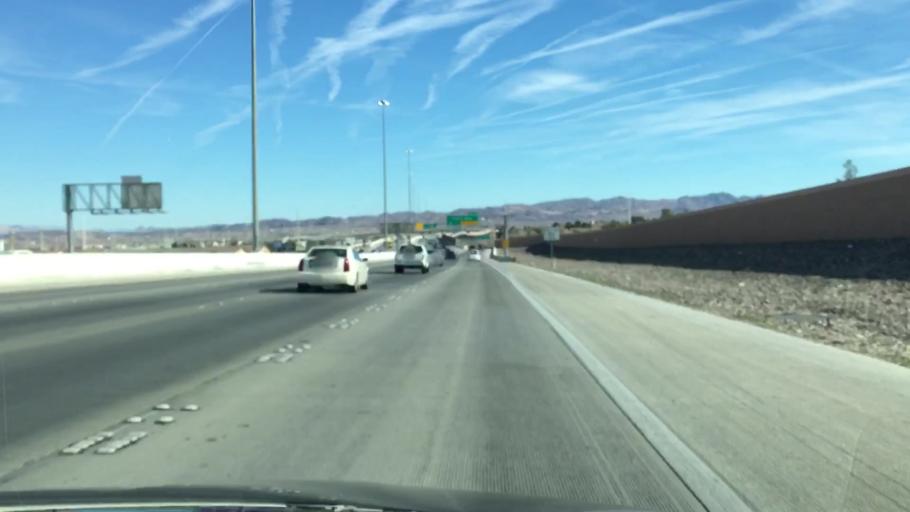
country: US
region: Nevada
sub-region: Clark County
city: Henderson
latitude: 36.0306
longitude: -115.0367
